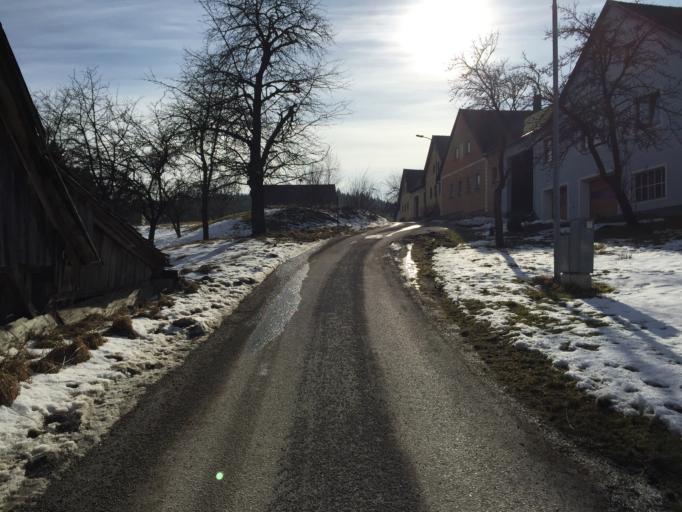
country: AT
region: Lower Austria
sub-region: Politischer Bezirk Gmund
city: Weitra
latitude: 48.6661
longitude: 14.9331
